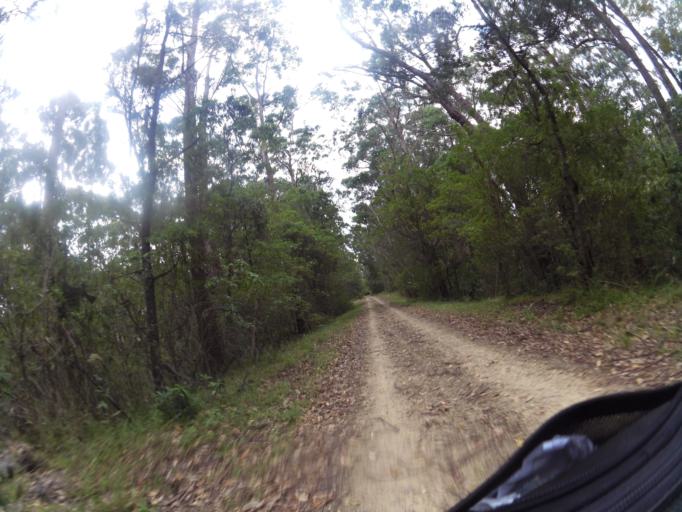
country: AU
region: Victoria
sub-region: East Gippsland
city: Lakes Entrance
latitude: -37.7315
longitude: 148.4266
